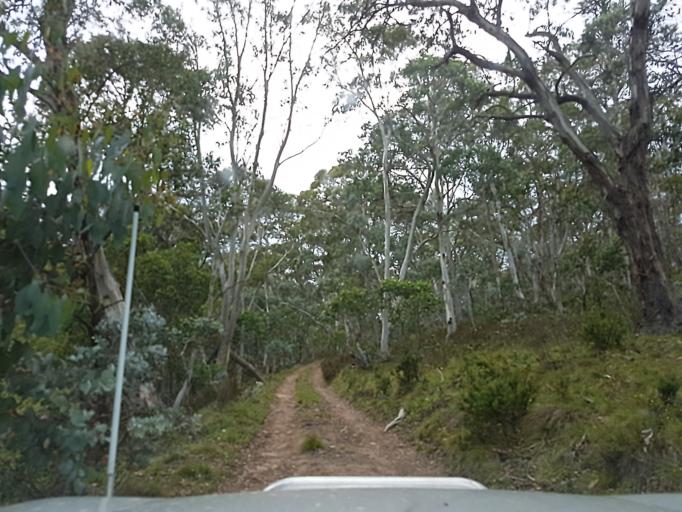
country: AU
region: New South Wales
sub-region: Snowy River
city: Jindabyne
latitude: -36.8876
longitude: 148.1262
